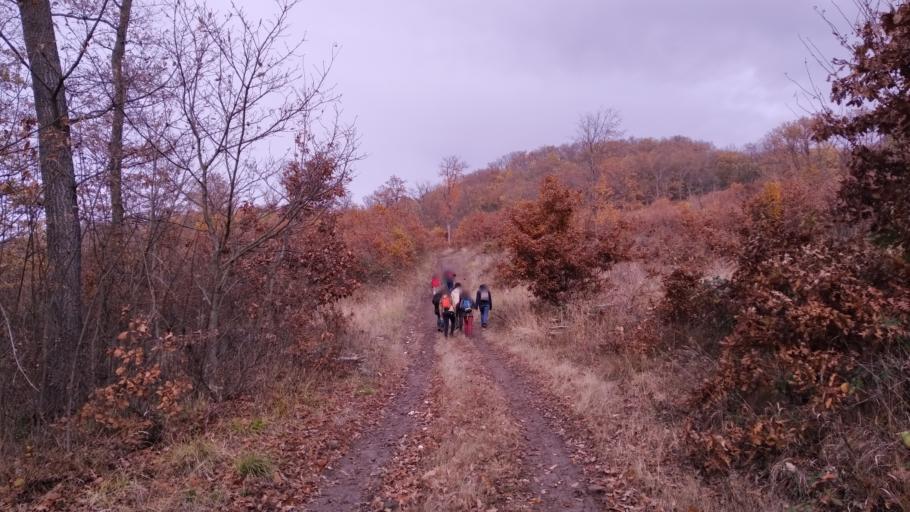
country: HU
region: Pest
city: Csobanka
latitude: 47.6743
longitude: 18.9592
